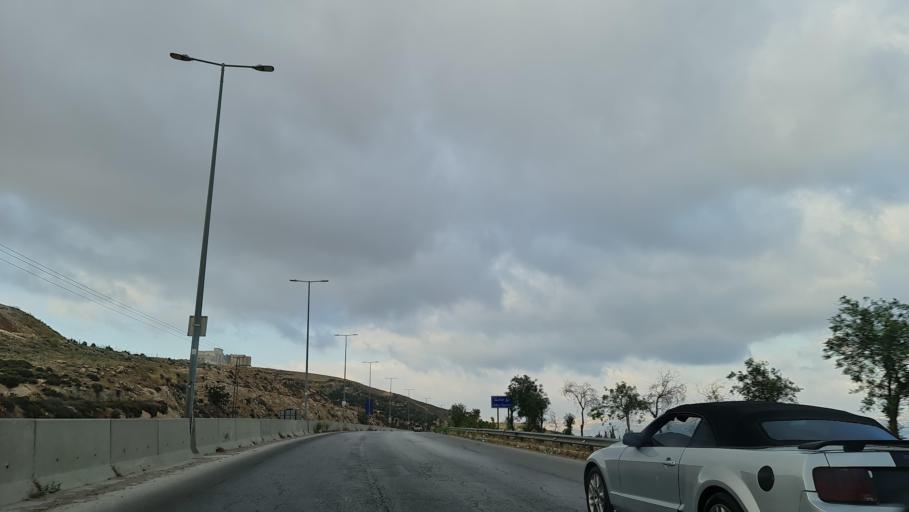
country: JO
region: Amman
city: Al Jubayhah
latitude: 32.0875
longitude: 35.8926
